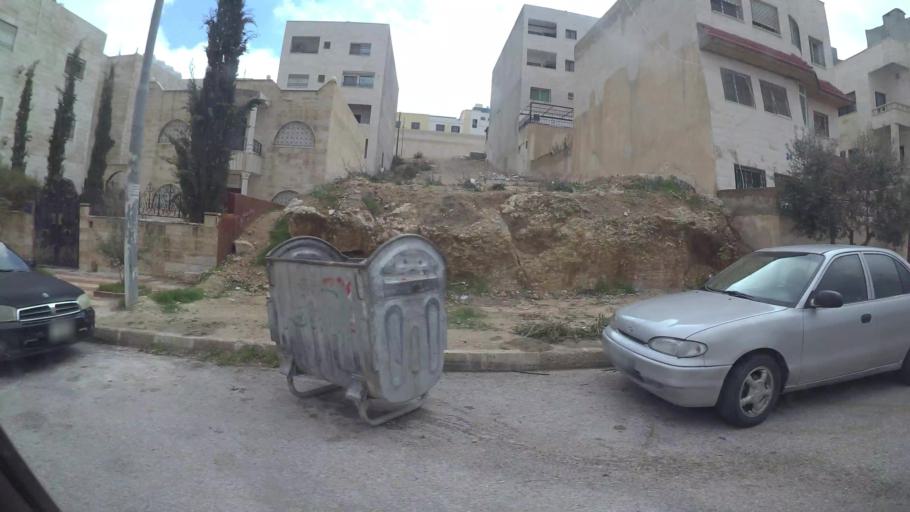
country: JO
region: Amman
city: Al Jubayhah
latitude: 32.0682
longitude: 35.8809
